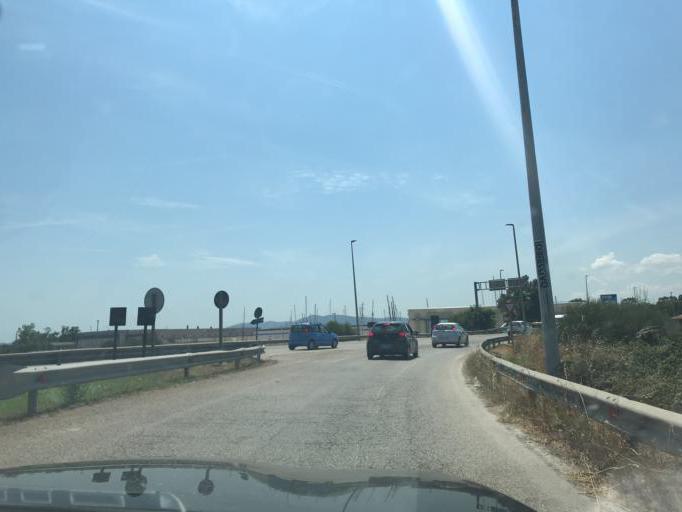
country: IT
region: Sardinia
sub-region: Provincia di Olbia-Tempio
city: Olbia
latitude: 40.9321
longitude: 9.5080
